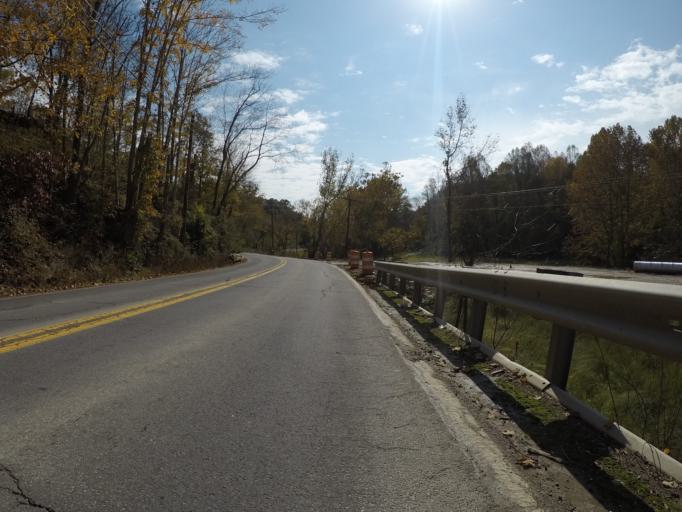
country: US
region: West Virginia
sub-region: Cabell County
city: Pea Ridge
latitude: 38.3845
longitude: -82.3786
